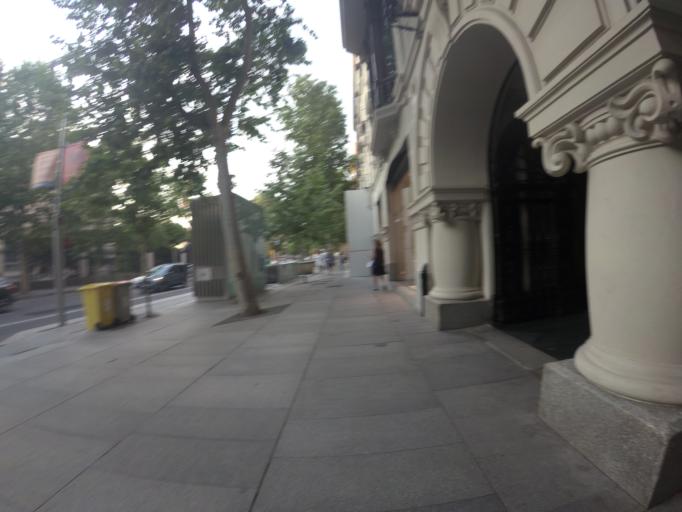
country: ES
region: Madrid
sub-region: Provincia de Madrid
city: Salamanca
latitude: 40.4235
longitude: -3.6881
